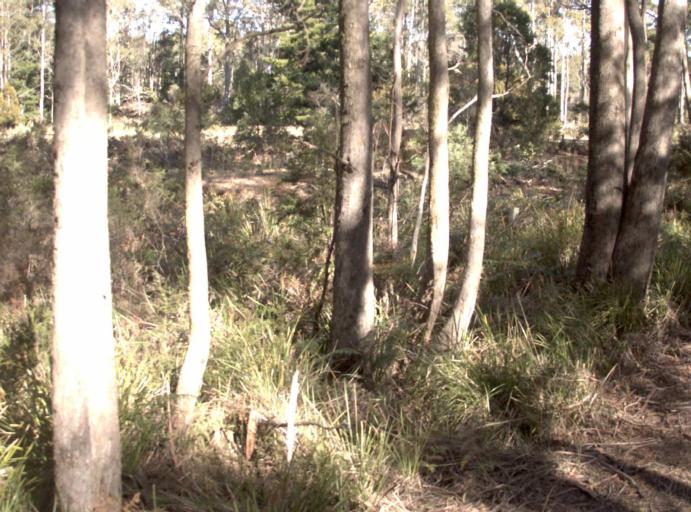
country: AU
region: Tasmania
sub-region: Launceston
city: Mayfield
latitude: -41.3106
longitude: 147.2048
